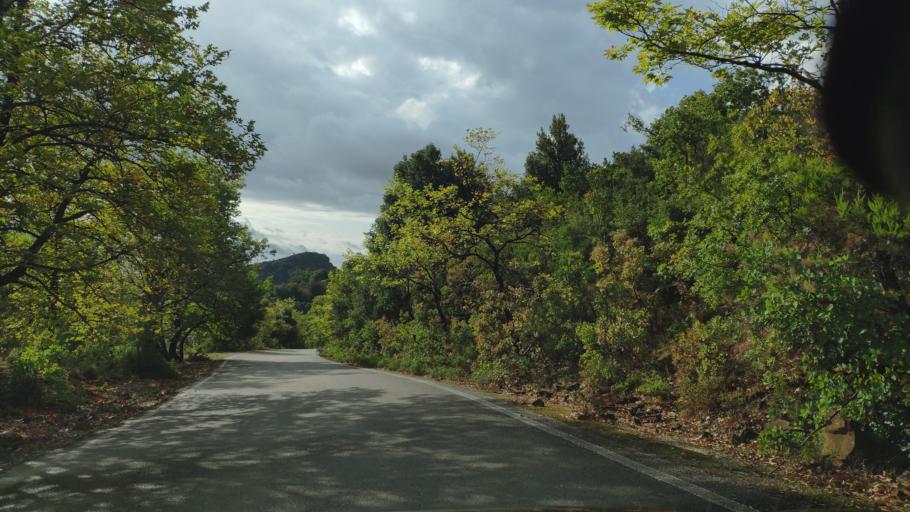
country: GR
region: West Greece
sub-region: Nomos Aitolias kai Akarnanias
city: Sardinia
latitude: 38.8611
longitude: 21.3037
